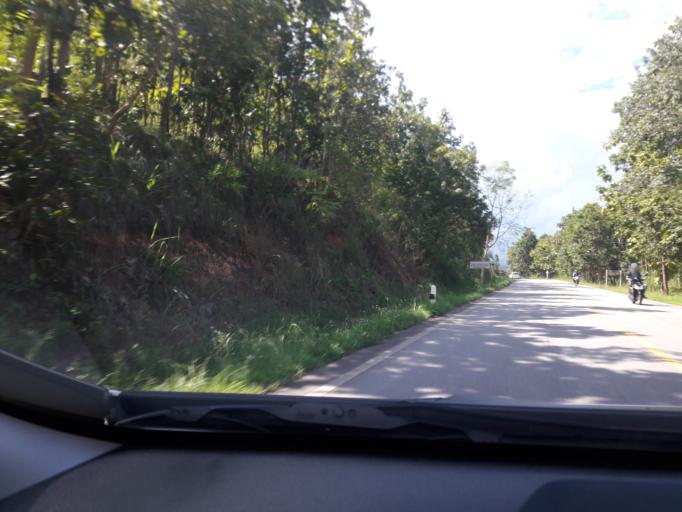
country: TH
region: Mae Hong Son
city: Mae Hi
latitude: 19.3048
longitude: 98.4548
